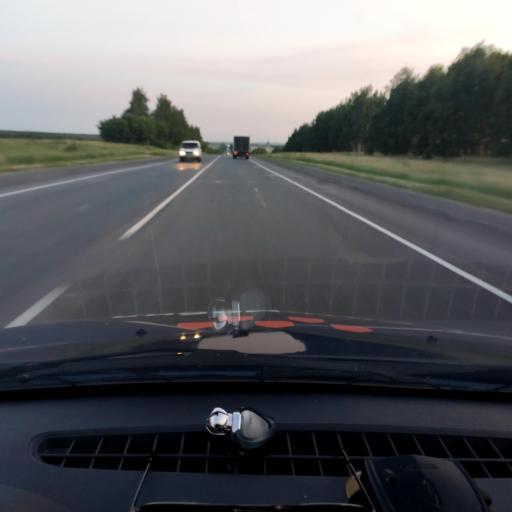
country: RU
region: Kursk
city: Gorshechnoye
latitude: 51.4536
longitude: 37.9181
